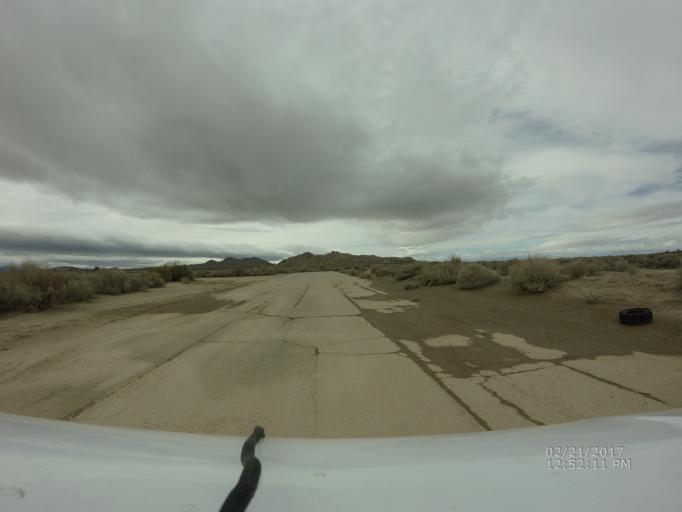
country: US
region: California
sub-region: Los Angeles County
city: Lake Los Angeles
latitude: 34.6422
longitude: -117.8532
